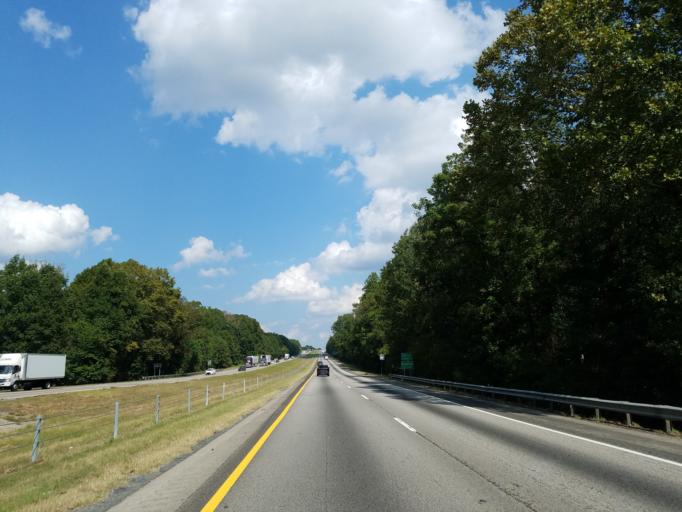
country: US
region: Georgia
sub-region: Jackson County
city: Hoschton
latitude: 34.0917
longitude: -83.8292
